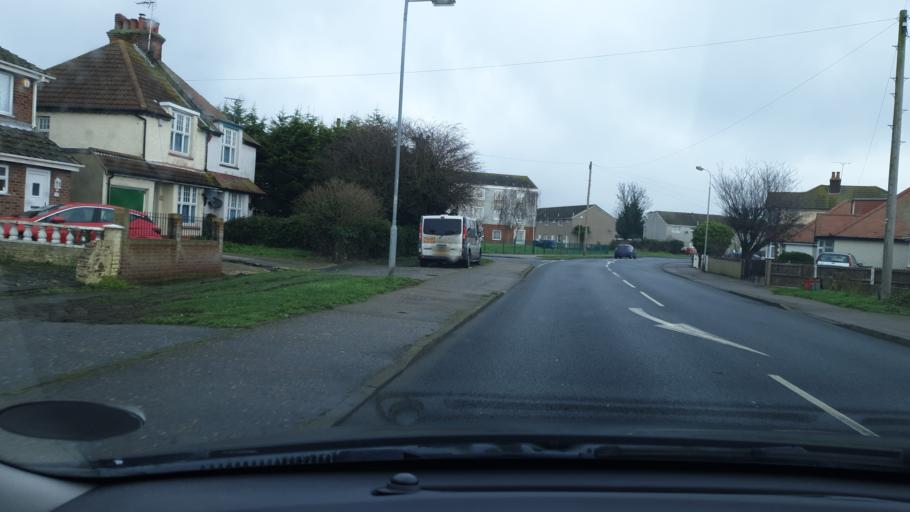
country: GB
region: England
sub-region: Essex
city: Clacton-on-Sea
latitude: 51.7958
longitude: 1.1305
